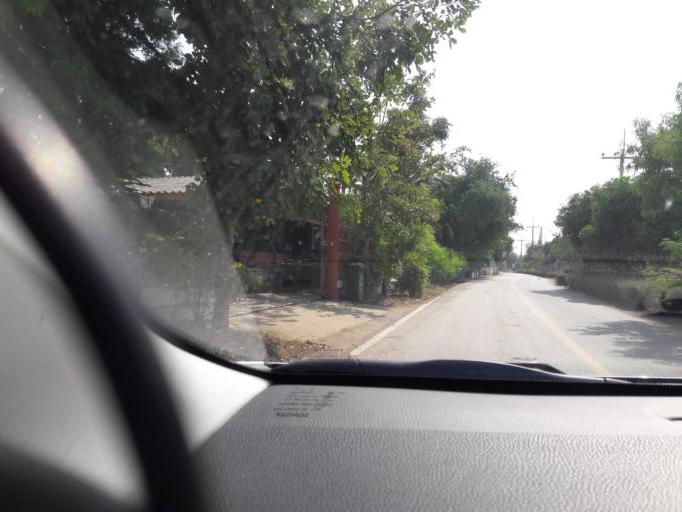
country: TH
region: Ang Thong
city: Pa Mok
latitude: 14.5330
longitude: 100.3935
